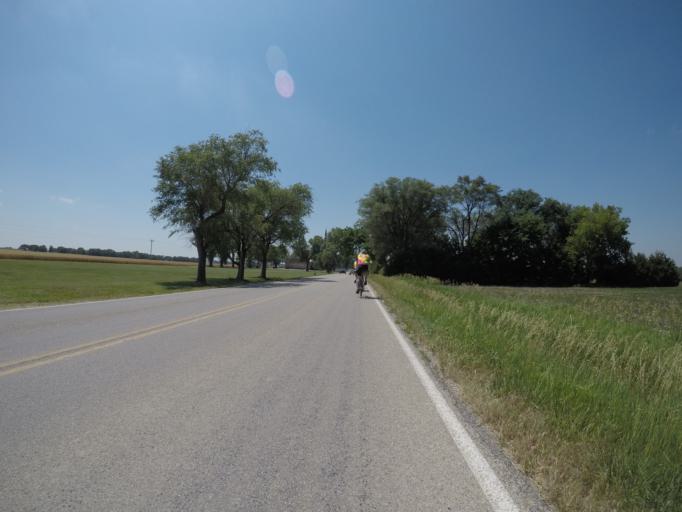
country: US
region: Kansas
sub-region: Pottawatomie County
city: Westmoreland
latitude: 39.2972
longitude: -96.4407
